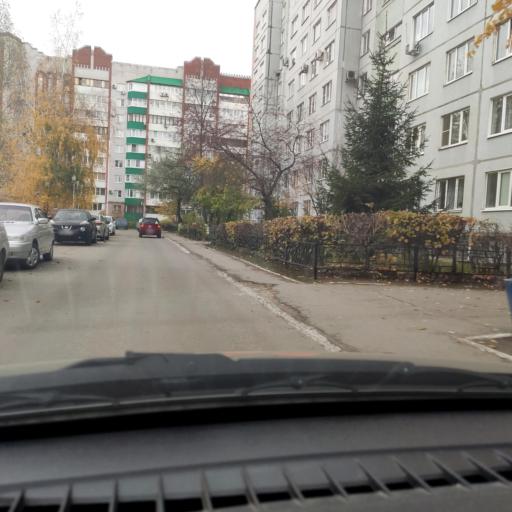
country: RU
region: Samara
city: Tol'yatti
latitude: 53.5387
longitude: 49.3234
